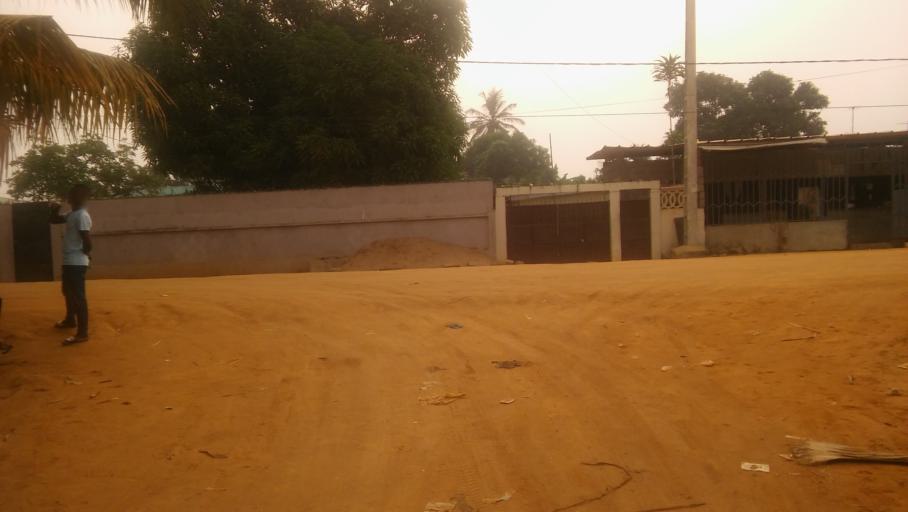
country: CI
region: Sud-Comoe
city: Grand-Bassam
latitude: 5.2021
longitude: -3.7337
